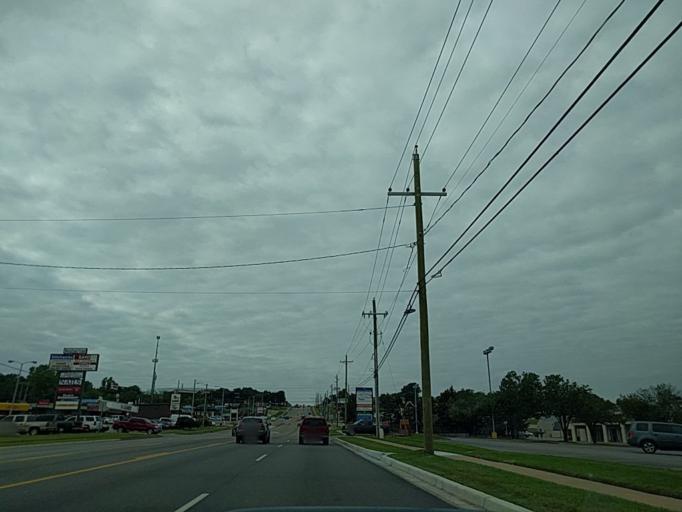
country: US
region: Oklahoma
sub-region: Tulsa County
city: Jenks
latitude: 36.0773
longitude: -95.9044
